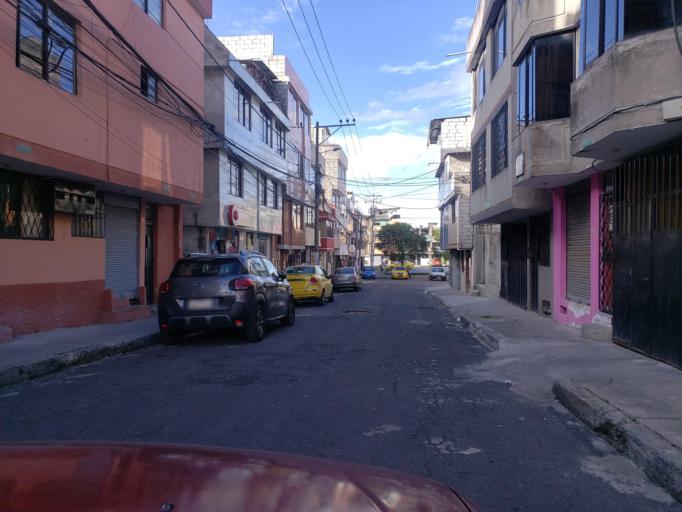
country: EC
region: Pichincha
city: Quito
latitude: -0.2668
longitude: -78.5403
